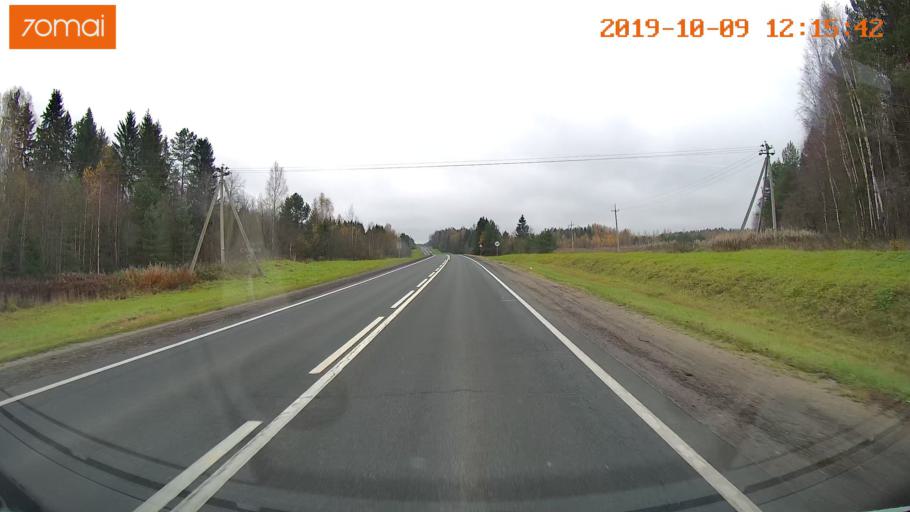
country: RU
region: Jaroslavl
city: Prechistoye
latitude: 58.4794
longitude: 40.3227
